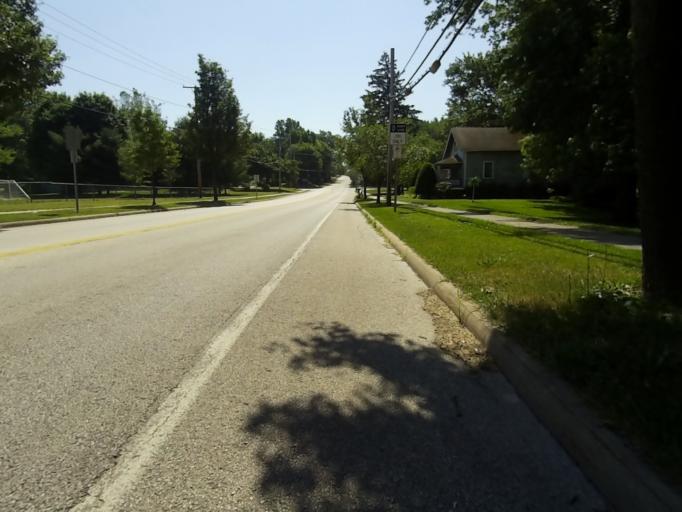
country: US
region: Ohio
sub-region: Portage County
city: Kent
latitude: 41.1616
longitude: -81.3690
